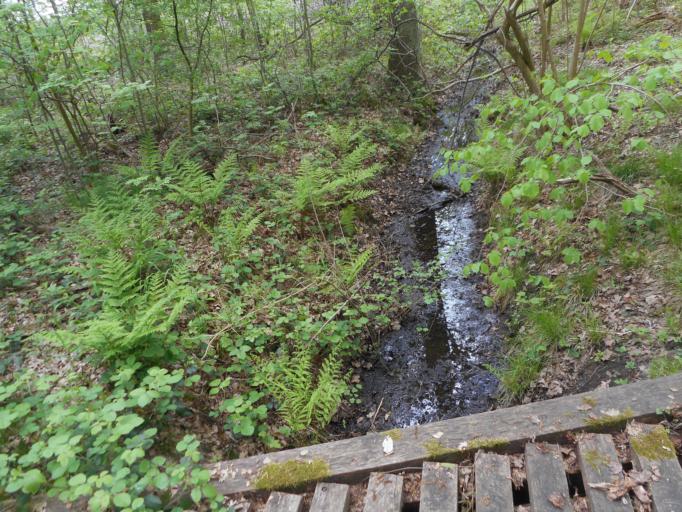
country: BE
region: Flanders
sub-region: Provincie Antwerpen
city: Sint-Katelijne-Waver
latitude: 51.0818
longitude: 4.5765
